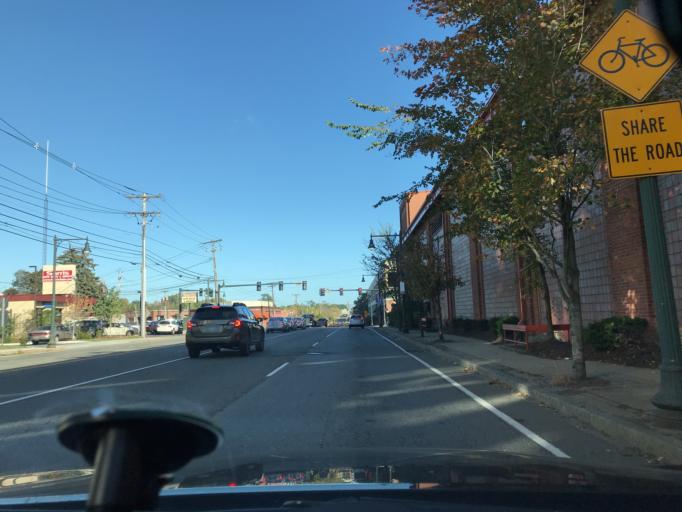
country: US
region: Massachusetts
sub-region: Middlesex County
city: Watertown
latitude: 42.3625
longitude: -71.1548
